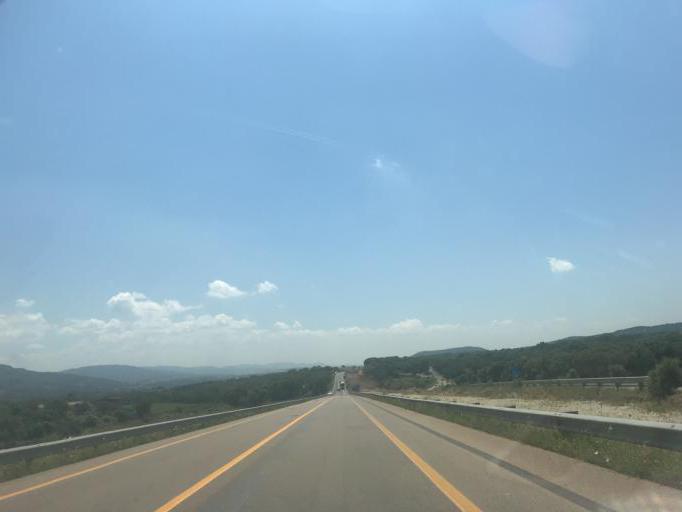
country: IT
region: Sardinia
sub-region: Provincia di Olbia-Tempio
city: Monti
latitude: 40.7982
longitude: 9.2735
